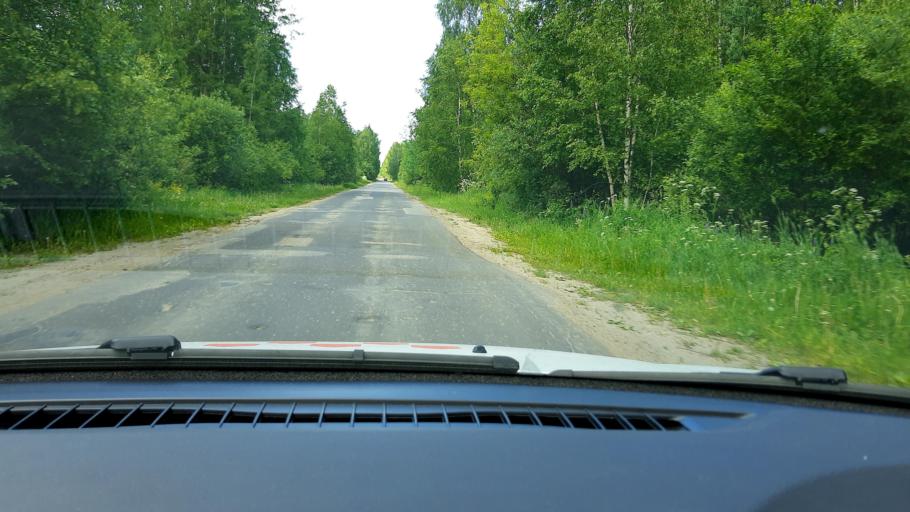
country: RU
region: Nizjnij Novgorod
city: Linda
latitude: 56.5452
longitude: 44.0797
